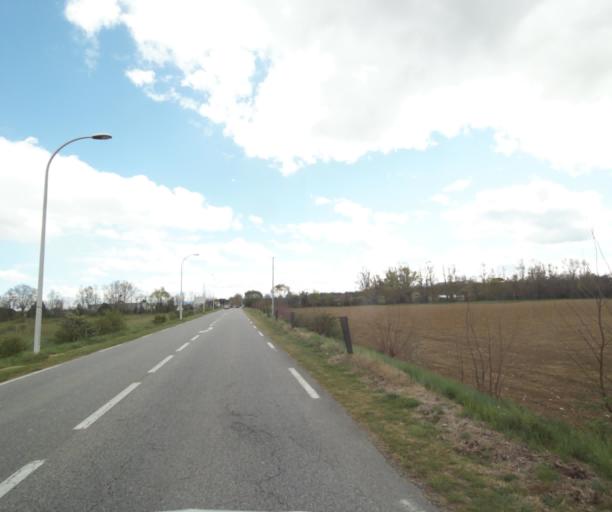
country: FR
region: Midi-Pyrenees
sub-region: Departement de l'Ariege
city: Saverdun
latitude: 43.2492
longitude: 1.5673
